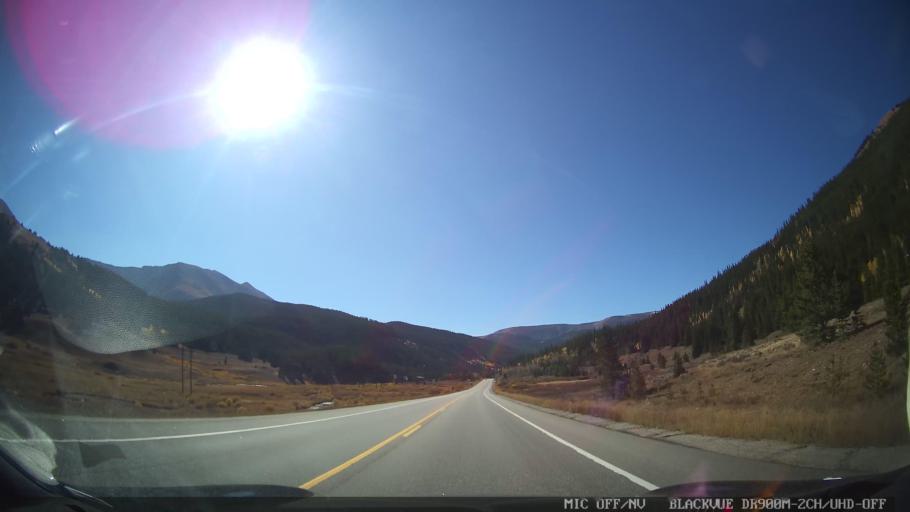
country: US
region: Colorado
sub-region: Lake County
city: Leadville
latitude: 39.3358
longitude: -106.2200
